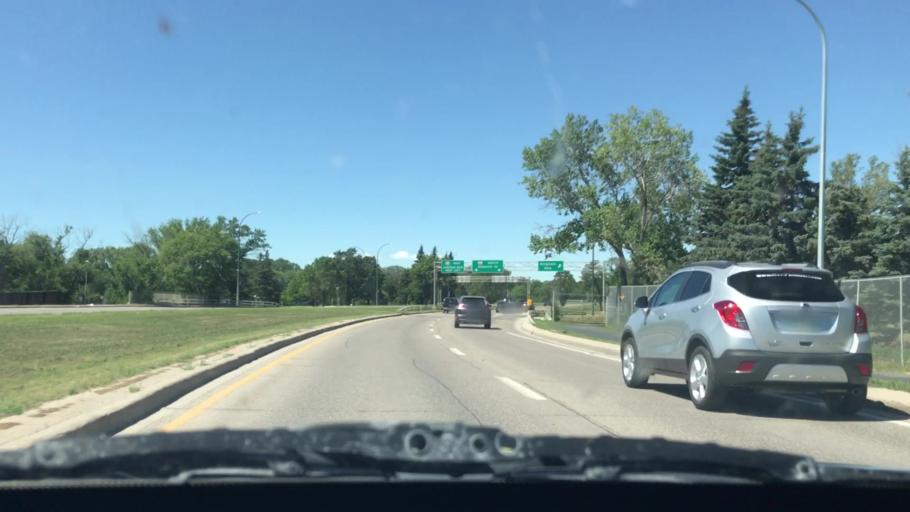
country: CA
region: Manitoba
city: Winnipeg
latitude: 49.8519
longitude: -97.1235
